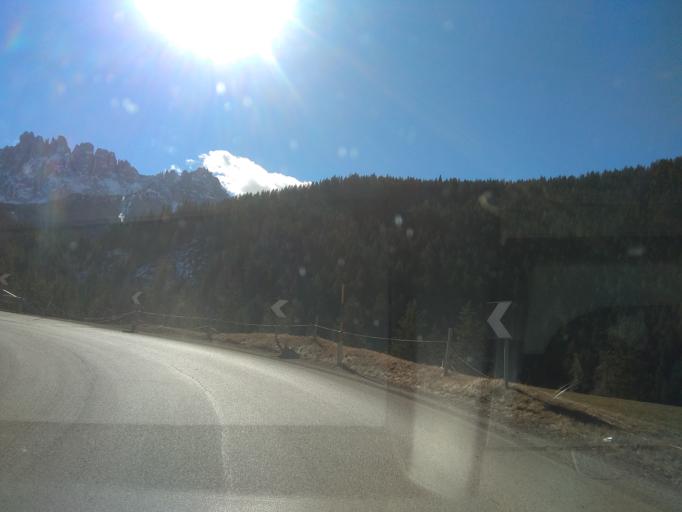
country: IT
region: Trentino-Alto Adige
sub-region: Bolzano
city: Nova Levante
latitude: 46.4206
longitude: 11.5578
